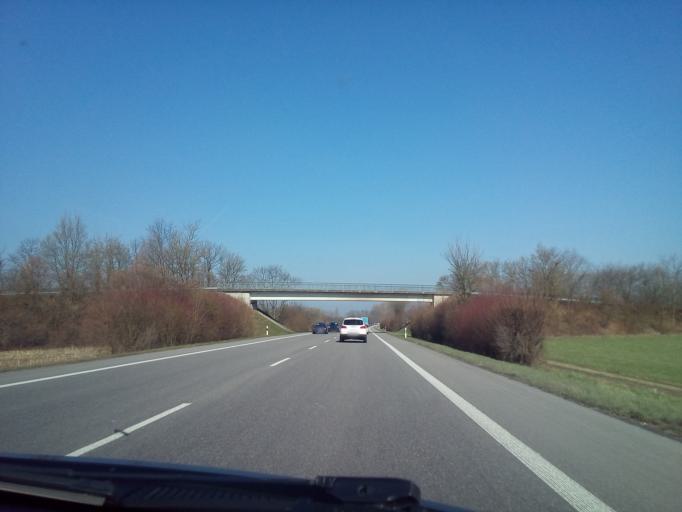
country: DE
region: Baden-Wuerttemberg
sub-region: Karlsruhe Region
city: Iffezheim
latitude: 48.8137
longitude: 8.1338
